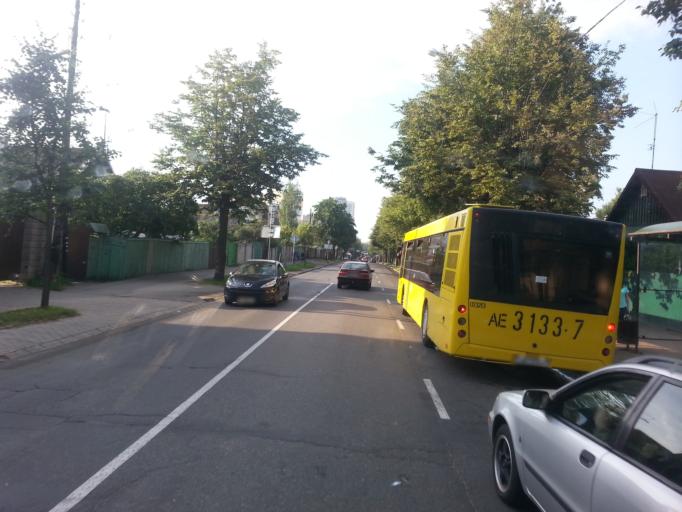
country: BY
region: Minsk
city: Minsk
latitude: 53.9344
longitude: 27.5463
